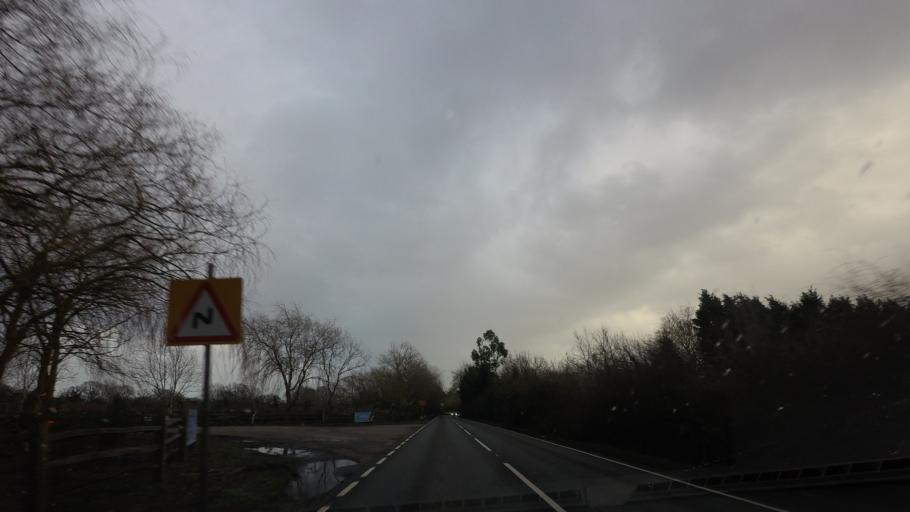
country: GB
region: England
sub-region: Kent
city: Staplehurst
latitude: 51.1912
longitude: 0.5415
